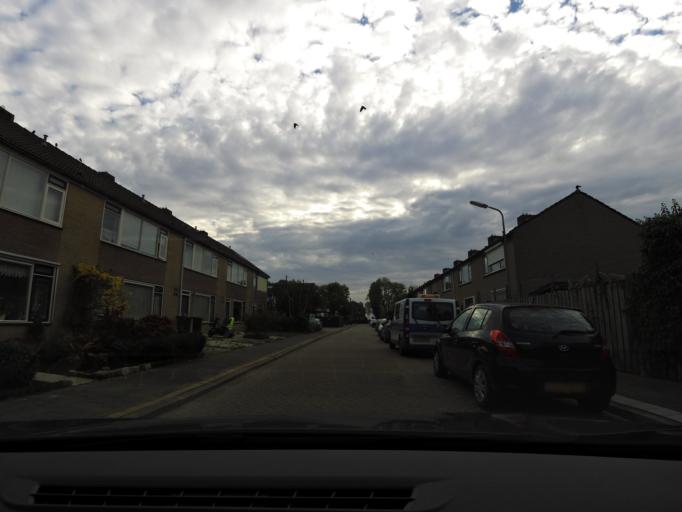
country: NL
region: South Holland
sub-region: Gemeente Goeree-Overflakkee
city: Middelharnis
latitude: 51.7126
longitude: 4.1712
